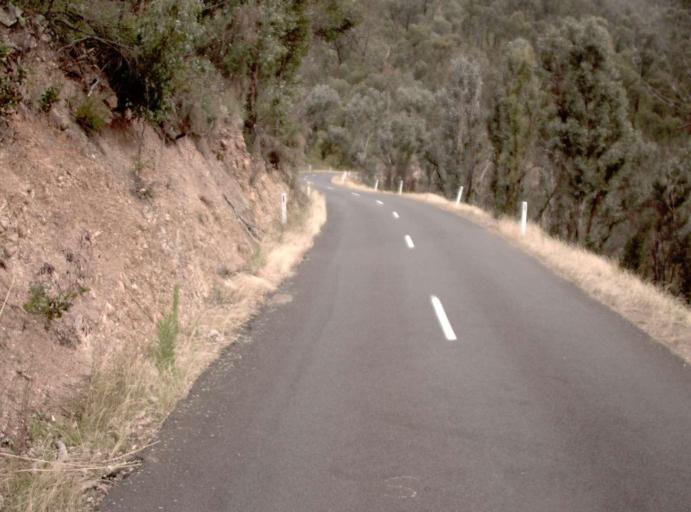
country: AU
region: Victoria
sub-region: Wellington
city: Heyfield
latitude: -37.7245
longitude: 146.6677
